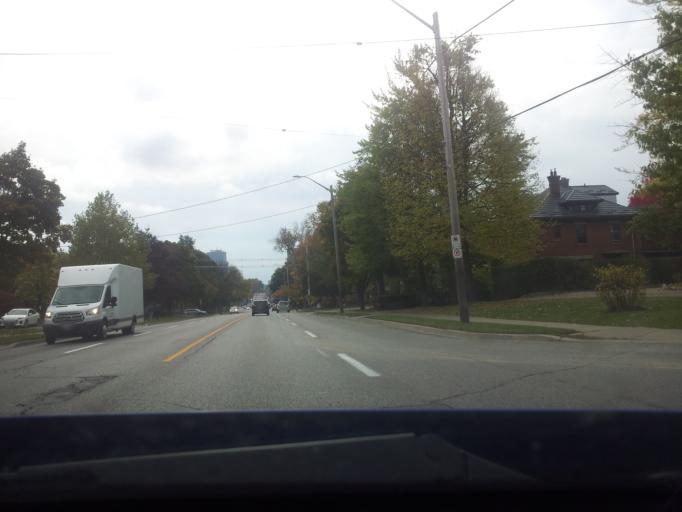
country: CA
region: Ontario
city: London
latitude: 42.9989
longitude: -81.2547
